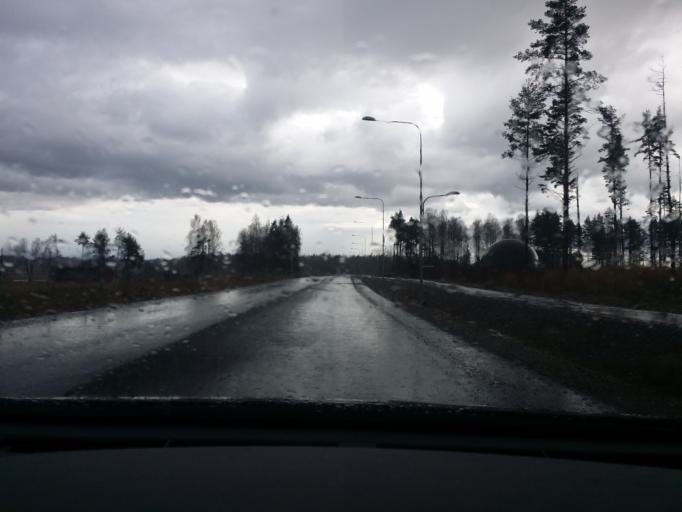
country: SE
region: Soedermanland
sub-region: Eskilstuna Kommun
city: Arla
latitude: 59.3459
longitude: 16.7018
